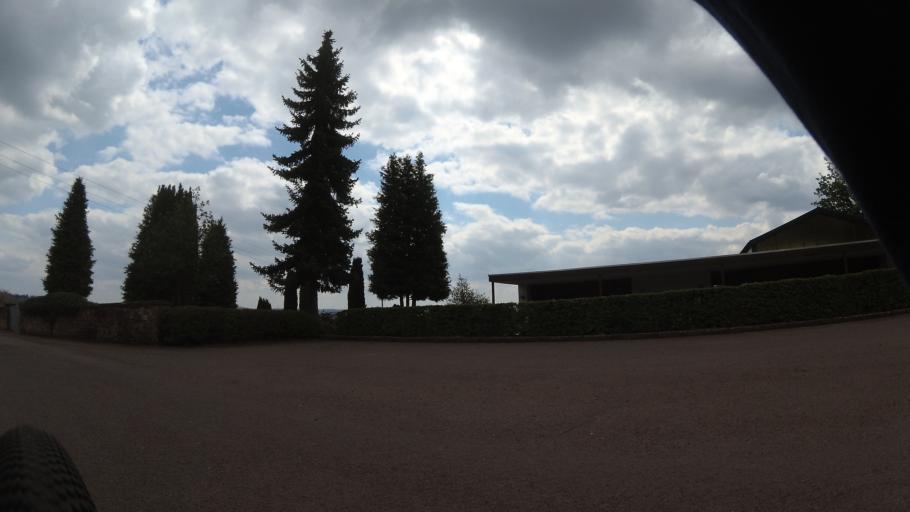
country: DE
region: Saarland
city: Britten
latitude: 49.5201
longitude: 6.6821
